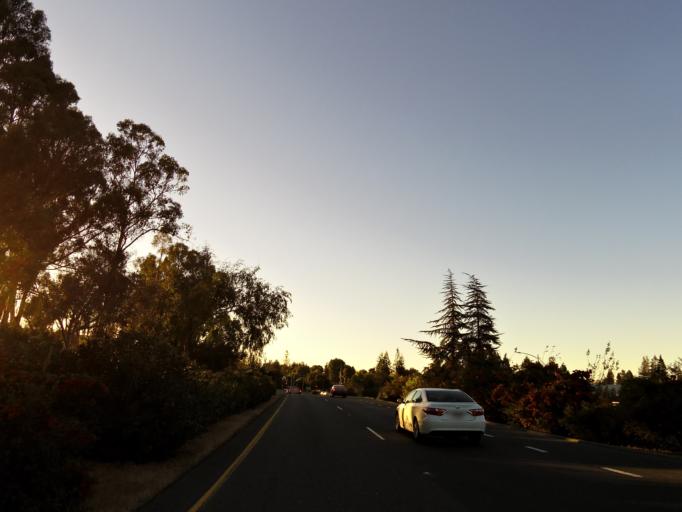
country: US
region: California
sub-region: Santa Clara County
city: Los Altos Hills
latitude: 37.4033
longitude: -122.1432
